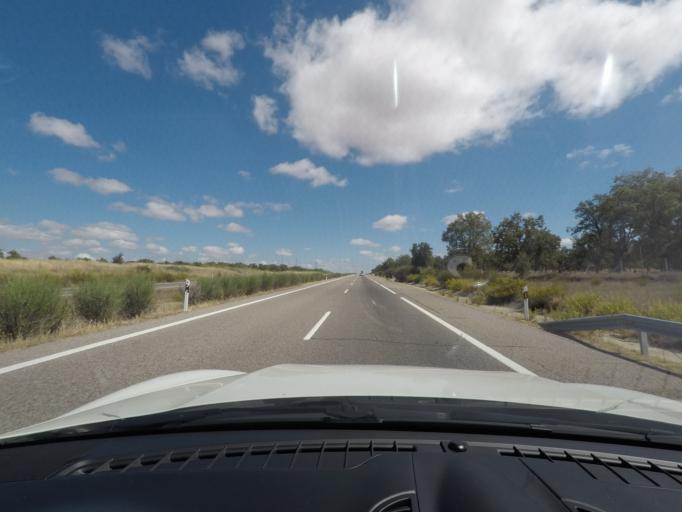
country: ES
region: Castille and Leon
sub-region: Provincia de Salamanca
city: Martin de Yeltes
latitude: 40.7538
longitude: -6.3280
